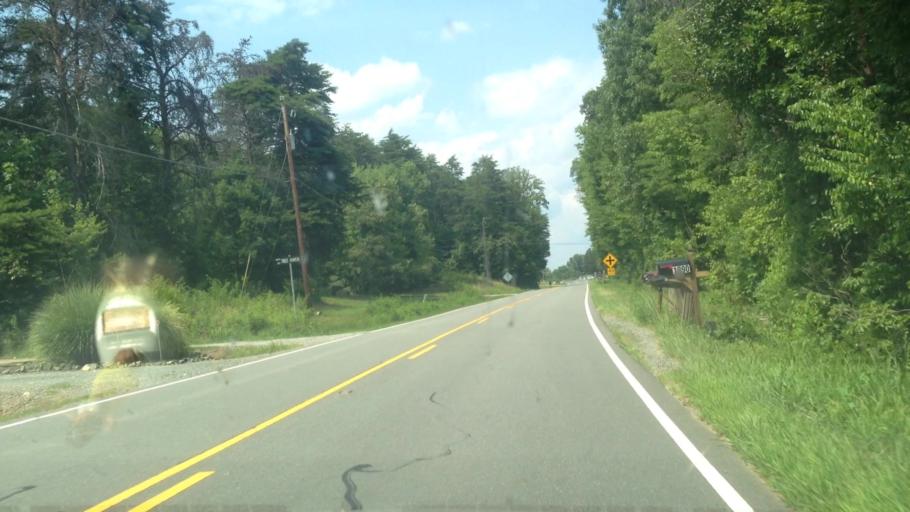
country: US
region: North Carolina
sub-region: Stokes County
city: Danbury
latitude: 36.3997
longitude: -80.0949
